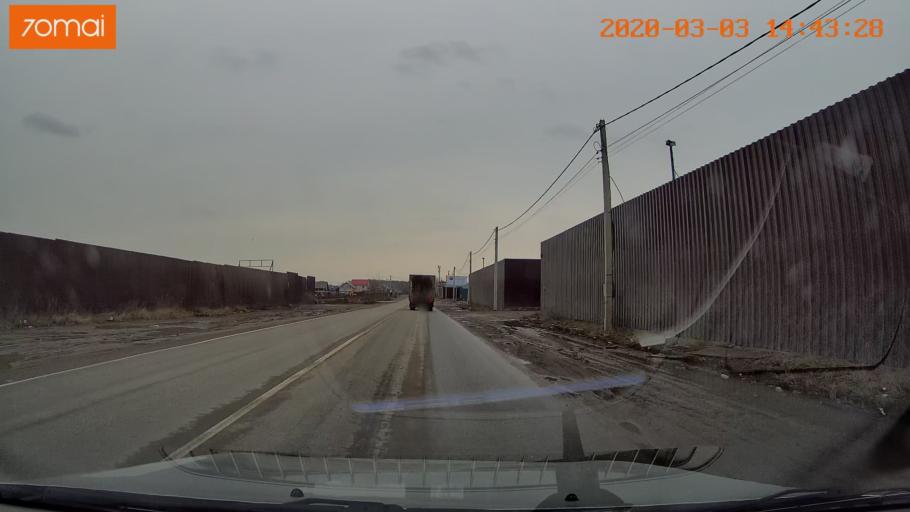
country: RU
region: Moskovskaya
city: Korenevo
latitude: 55.7014
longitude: 38.0200
